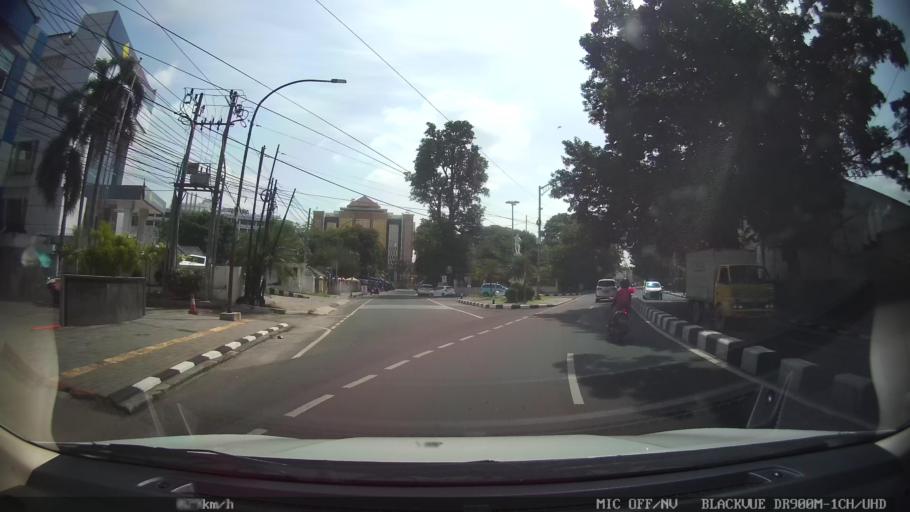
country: ID
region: North Sumatra
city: Medan
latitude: 3.5837
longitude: 98.6758
